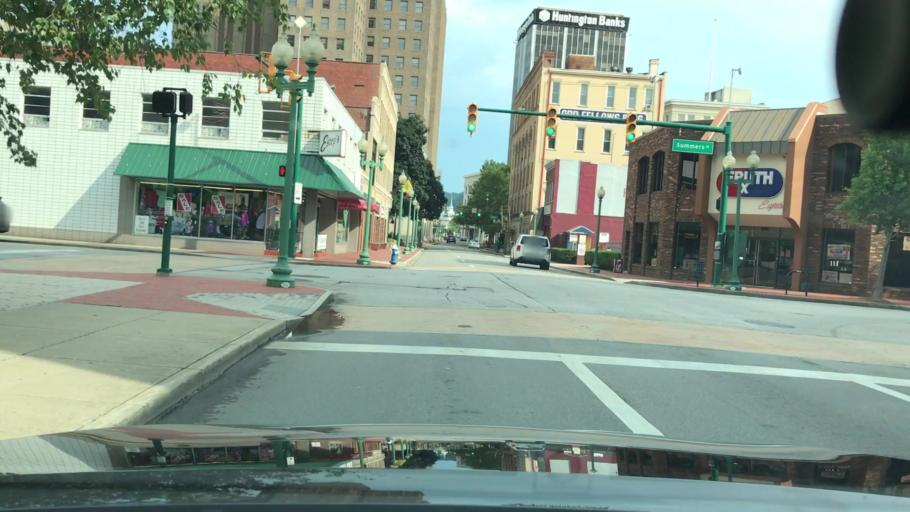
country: US
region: West Virginia
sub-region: Kanawha County
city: Charleston
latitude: 38.3519
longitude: -81.6341
